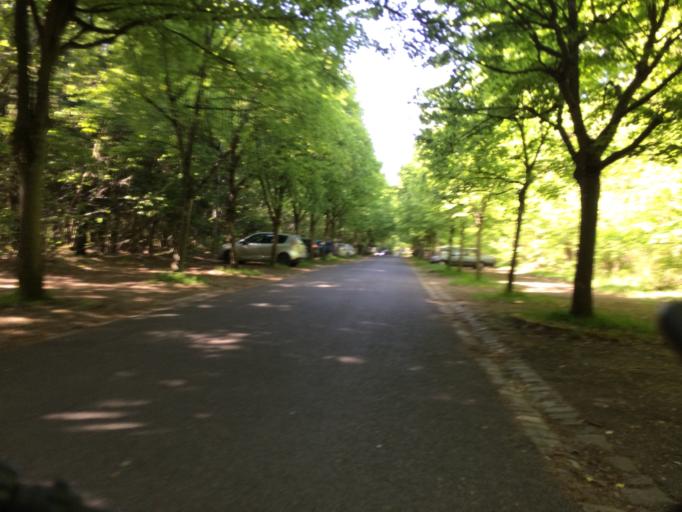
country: FR
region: Ile-de-France
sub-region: Departement de l'Essonne
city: Verrieres-le-Buisson
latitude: 48.7492
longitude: 2.2488
